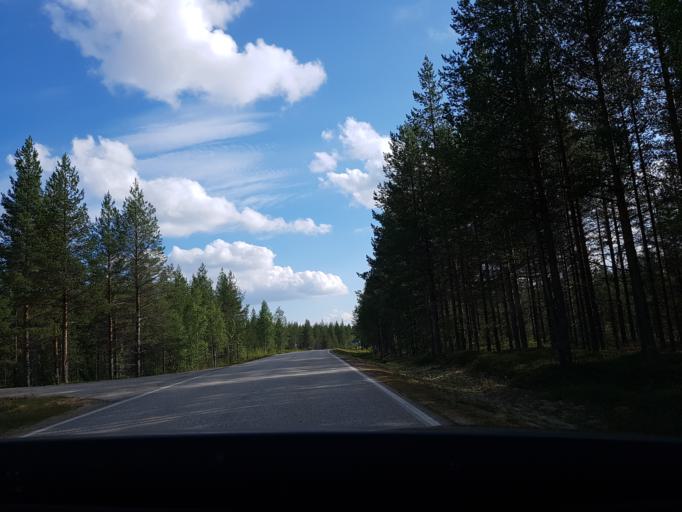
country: FI
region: Kainuu
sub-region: Kehys-Kainuu
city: Kuhmo
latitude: 64.6232
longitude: 29.6978
